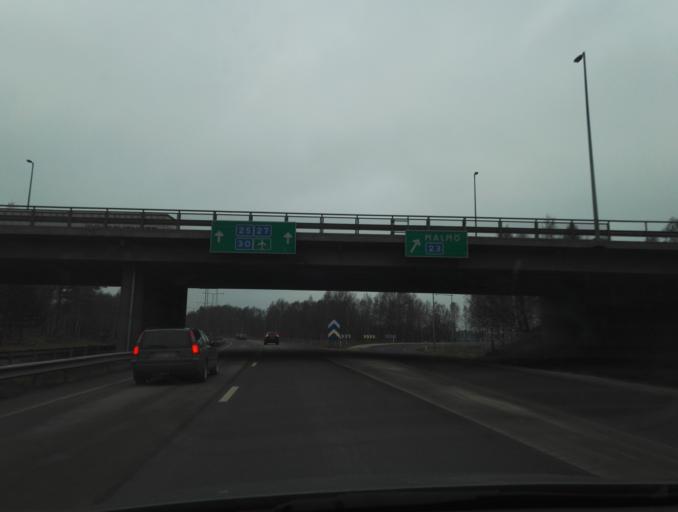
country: SE
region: Kronoberg
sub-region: Vaxjo Kommun
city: Vaexjoe
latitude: 56.8895
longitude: 14.7543
